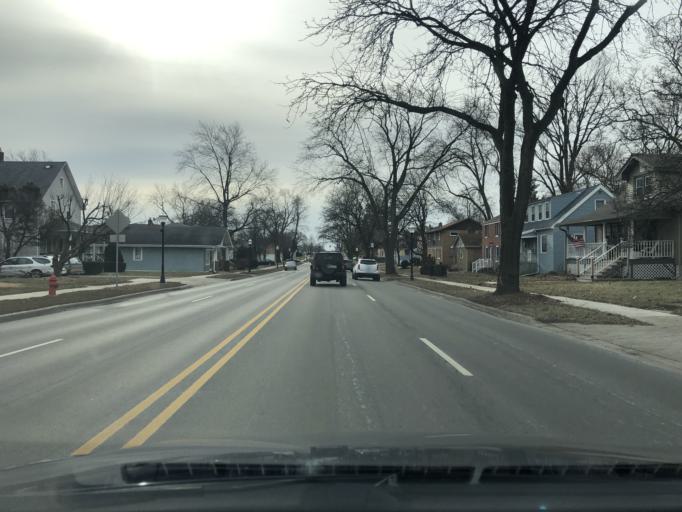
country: US
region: Illinois
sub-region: DuPage County
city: Bensenville
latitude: 41.9531
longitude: -87.9397
